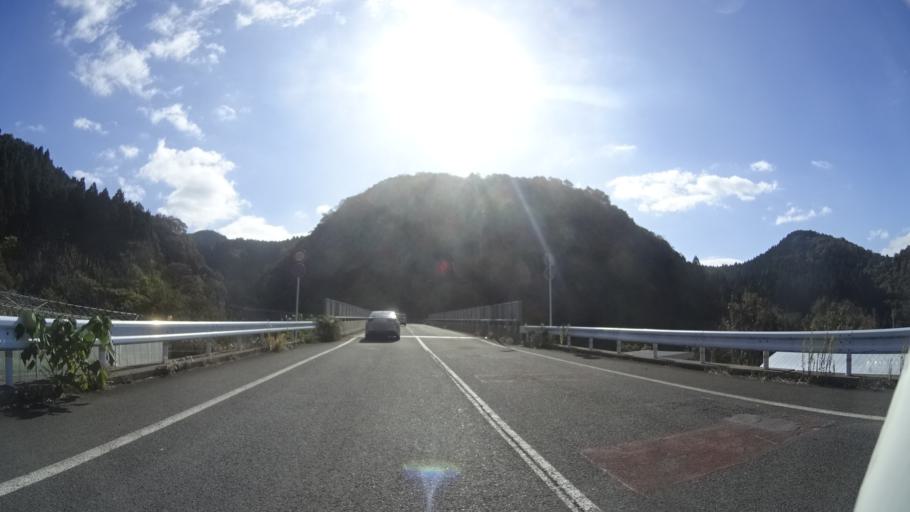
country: JP
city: Asahi
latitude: 35.9607
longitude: 135.9954
